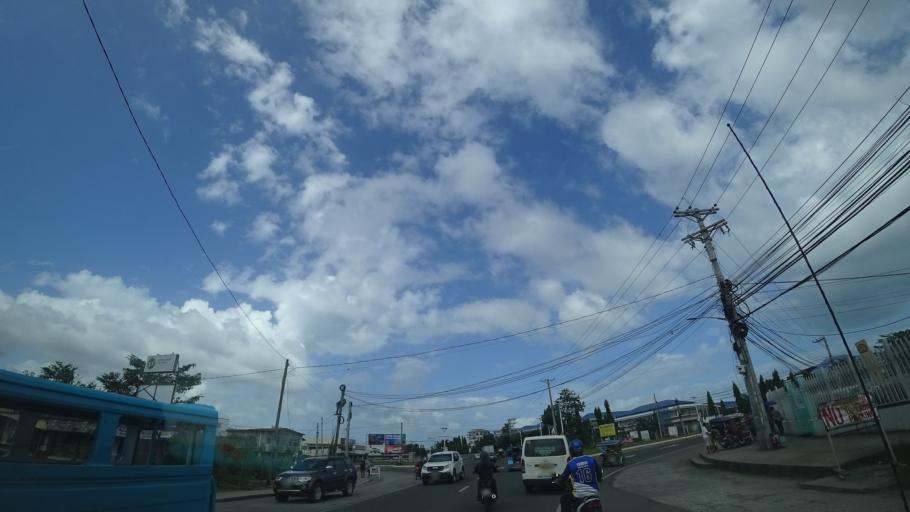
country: PH
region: Eastern Visayas
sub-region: Province of Leyte
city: Pawing
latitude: 11.1788
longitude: 125.0025
